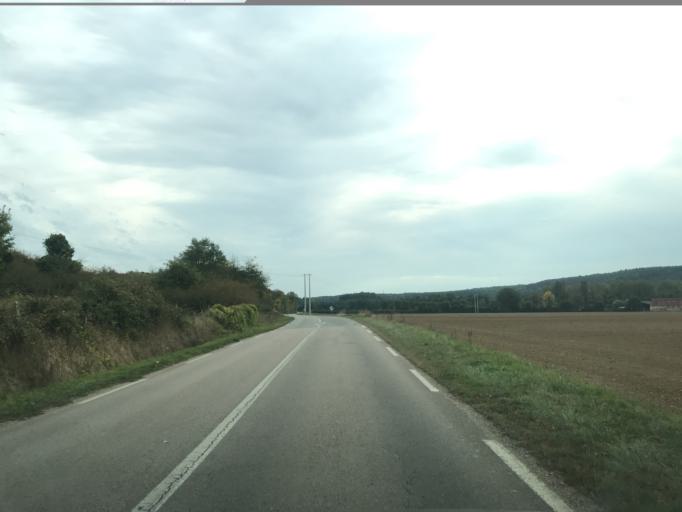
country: FR
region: Haute-Normandie
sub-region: Departement de l'Eure
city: Acquigny
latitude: 49.1897
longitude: 1.1821
